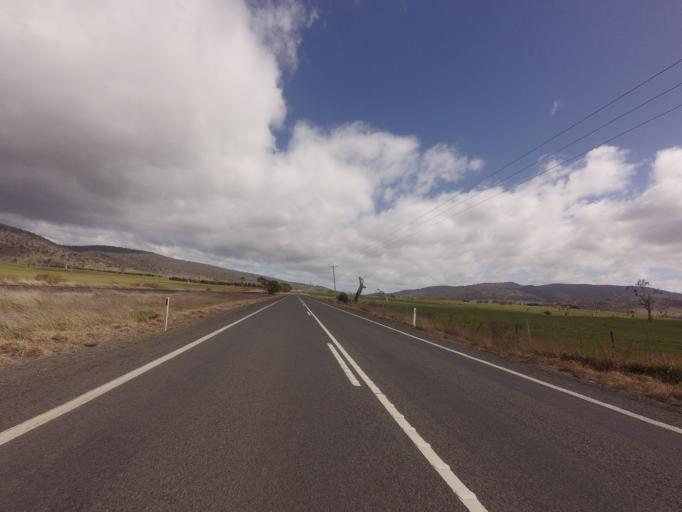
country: AU
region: Tasmania
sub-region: Northern Midlands
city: Evandale
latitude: -41.8101
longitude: 147.6506
